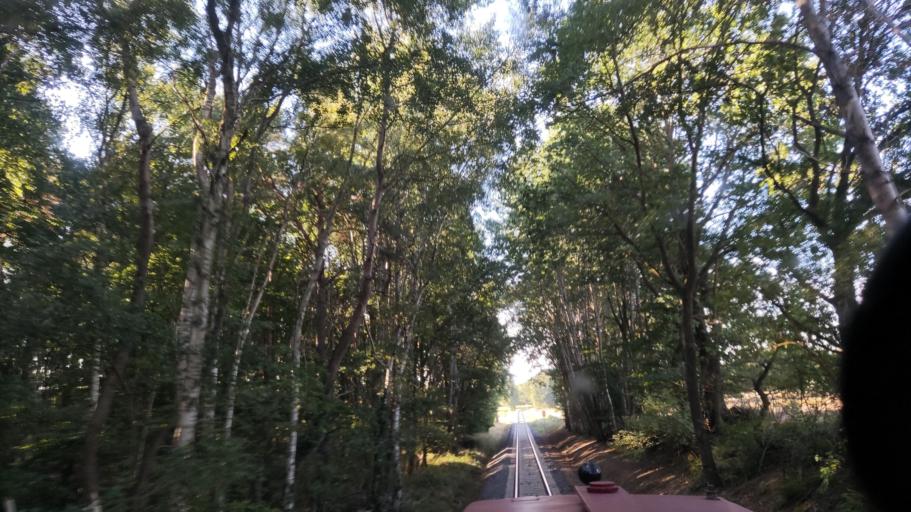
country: DE
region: Lower Saxony
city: Melbeck
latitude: 53.2018
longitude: 10.3797
